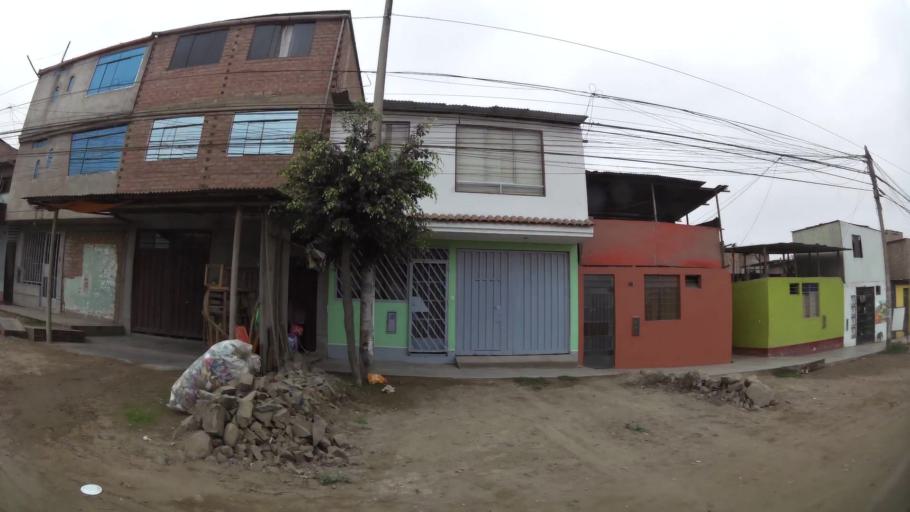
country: PE
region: Lima
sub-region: Lima
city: Surco
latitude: -12.2163
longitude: -76.9277
